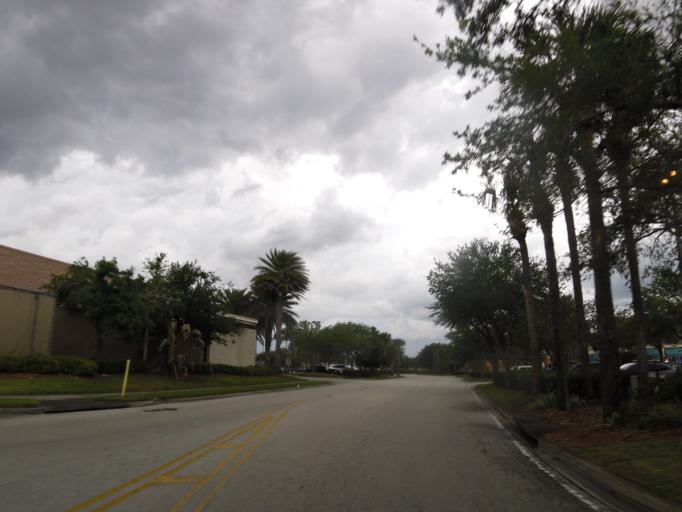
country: US
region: Florida
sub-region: Saint Johns County
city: Ponte Vedra Beach
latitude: 30.2533
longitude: -81.3895
